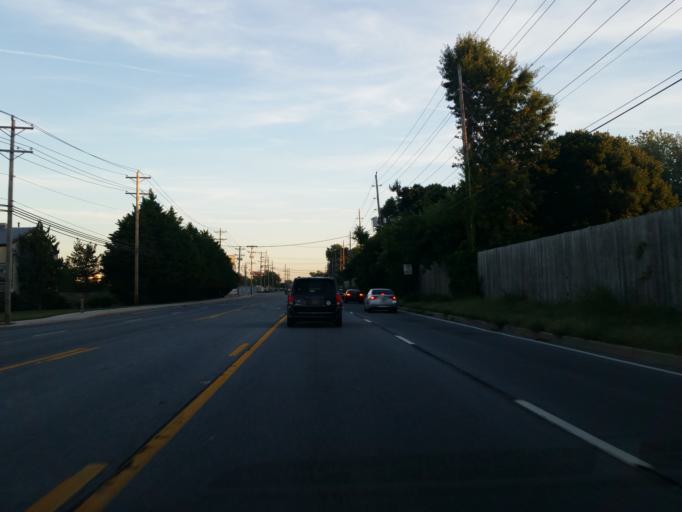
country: US
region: Delaware
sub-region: New Castle County
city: Brookside
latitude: 39.6555
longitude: -75.7342
